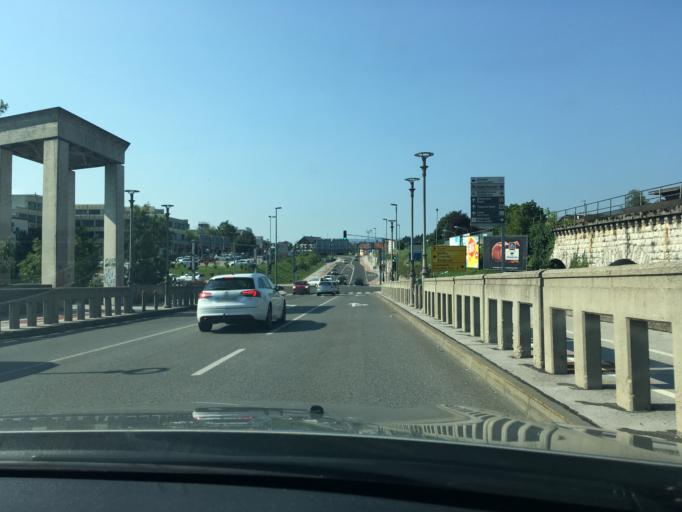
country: SI
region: Novo Mesto
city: Novo Mesto
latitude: 45.8030
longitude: 15.1620
